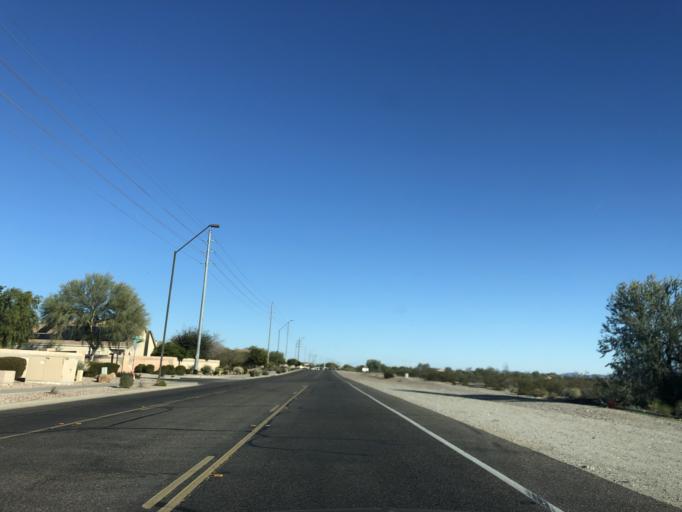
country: US
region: Arizona
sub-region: Maricopa County
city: Buckeye
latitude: 33.4355
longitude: -112.5710
